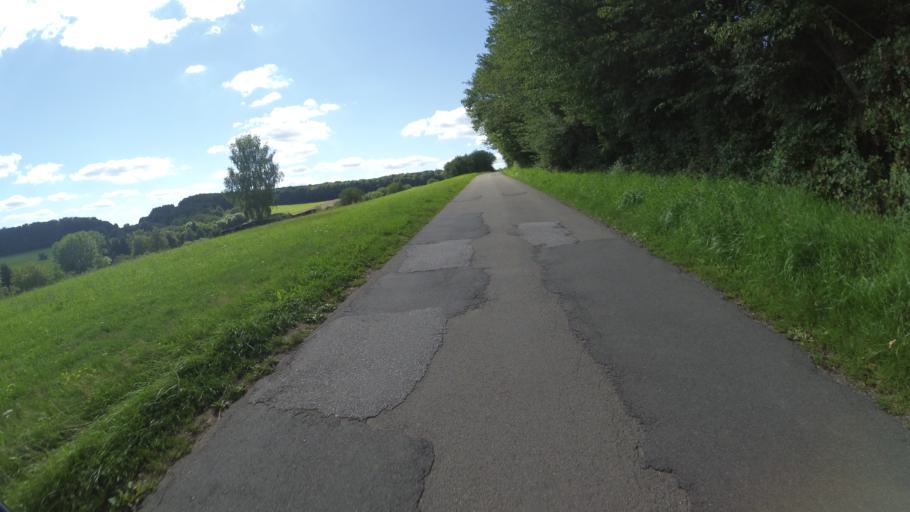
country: DE
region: Saarland
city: Marpingen
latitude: 49.4262
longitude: 7.0693
